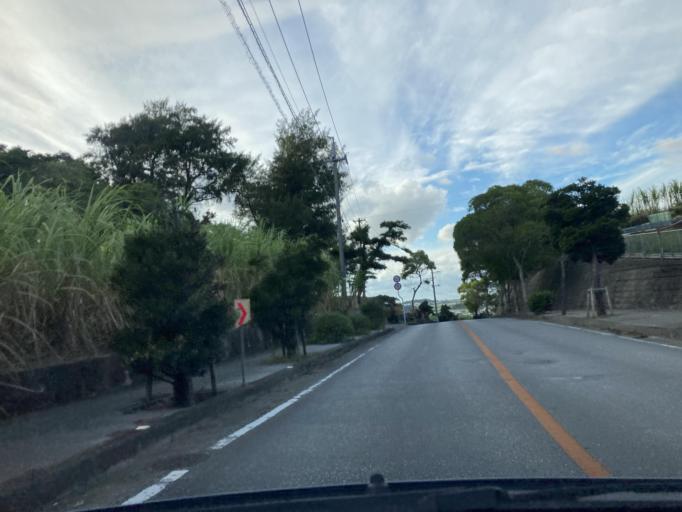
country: JP
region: Okinawa
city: Itoman
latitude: 26.1321
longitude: 127.7239
